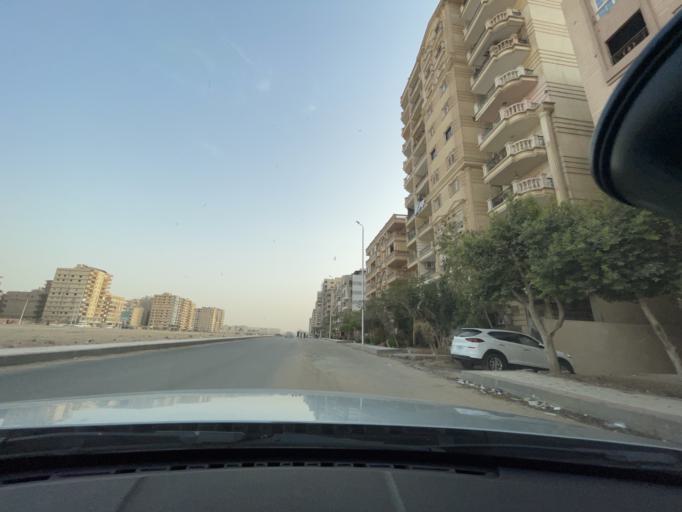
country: EG
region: Muhafazat al Qahirah
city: Cairo
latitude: 30.0527
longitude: 31.3698
